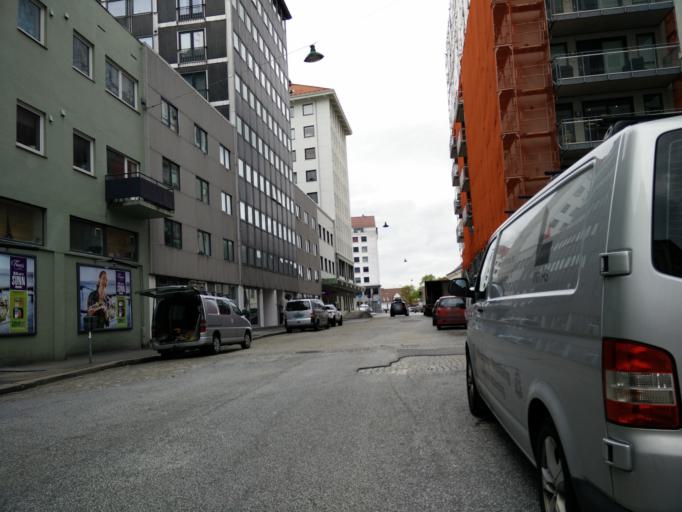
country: NO
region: Hordaland
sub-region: Bergen
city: Bergen
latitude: 60.3979
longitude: 5.3119
